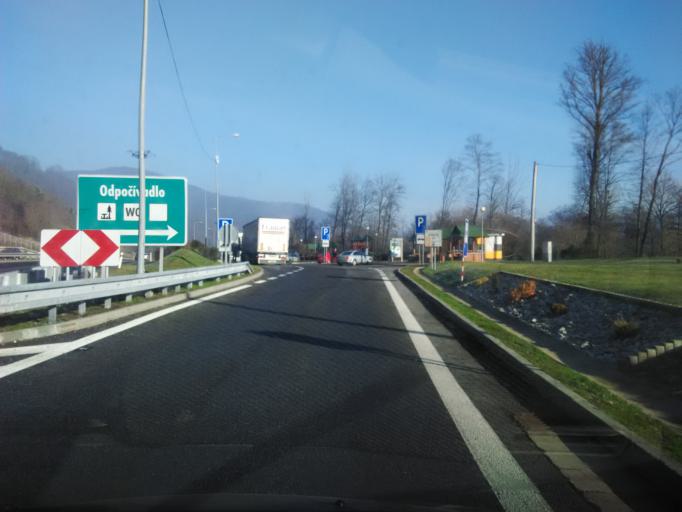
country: SK
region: Banskobystricky
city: Zarnovica
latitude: 48.4618
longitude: 18.6909
